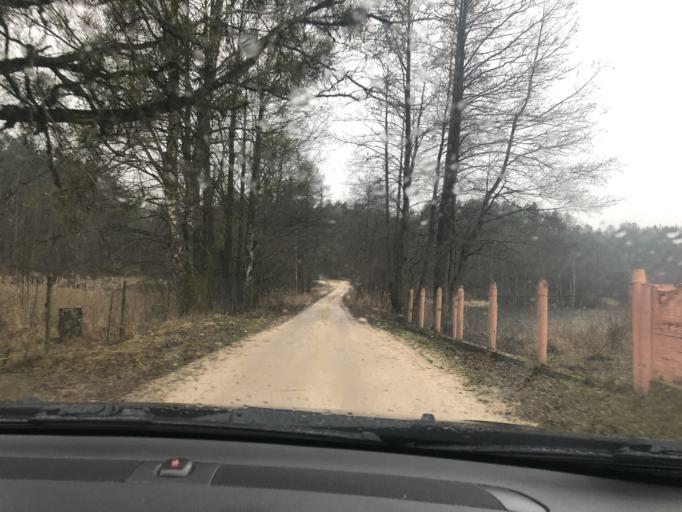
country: BY
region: Grodnenskaya
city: Skidal'
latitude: 53.8585
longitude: 24.2410
